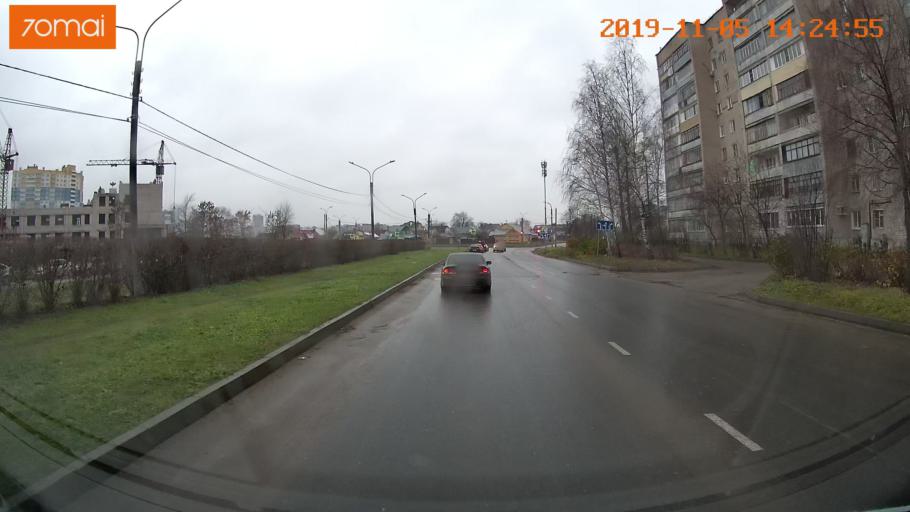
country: RU
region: Ivanovo
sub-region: Gorod Ivanovo
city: Ivanovo
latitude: 56.9704
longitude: 40.9945
